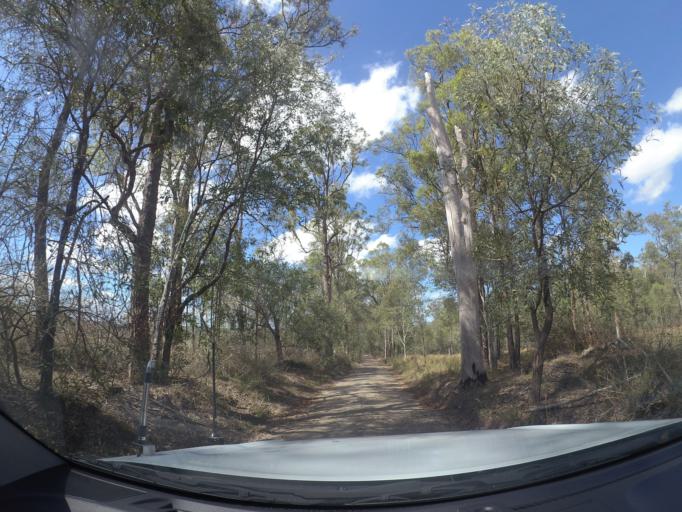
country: AU
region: Queensland
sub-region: Logan
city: Cedar Vale
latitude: -27.8401
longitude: 152.9744
